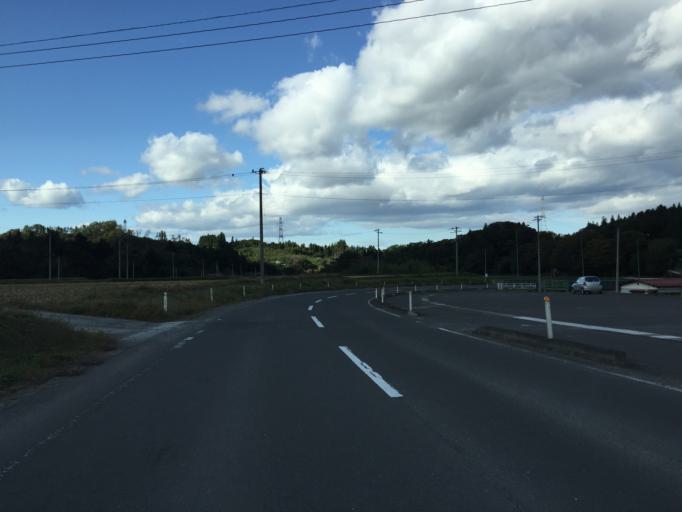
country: JP
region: Miyagi
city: Marumori
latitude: 37.8489
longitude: 140.8313
